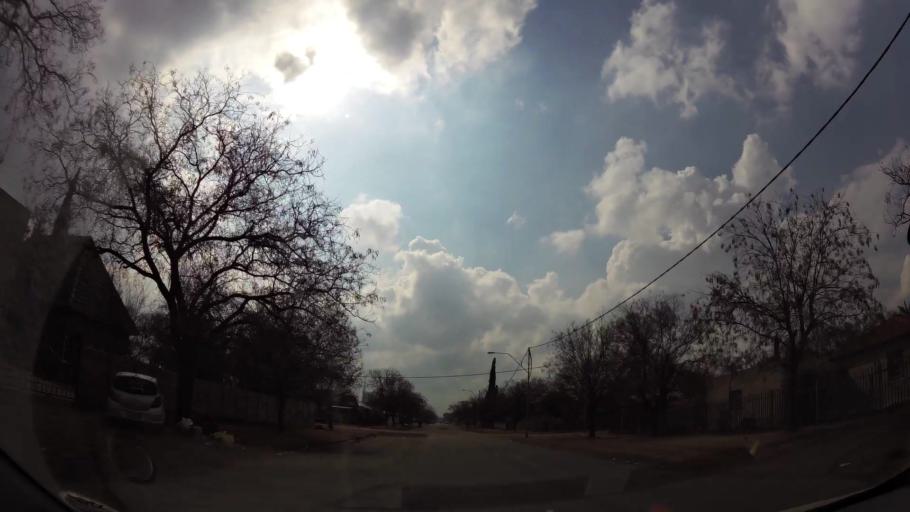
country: ZA
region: Gauteng
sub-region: Sedibeng District Municipality
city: Vereeniging
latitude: -26.6782
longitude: 27.9242
